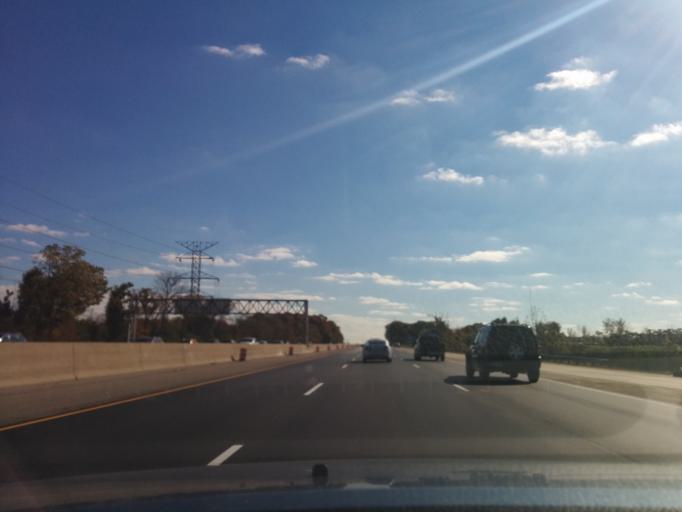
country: US
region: Michigan
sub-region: Oakland County
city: Novi
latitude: 42.4924
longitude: -83.5102
